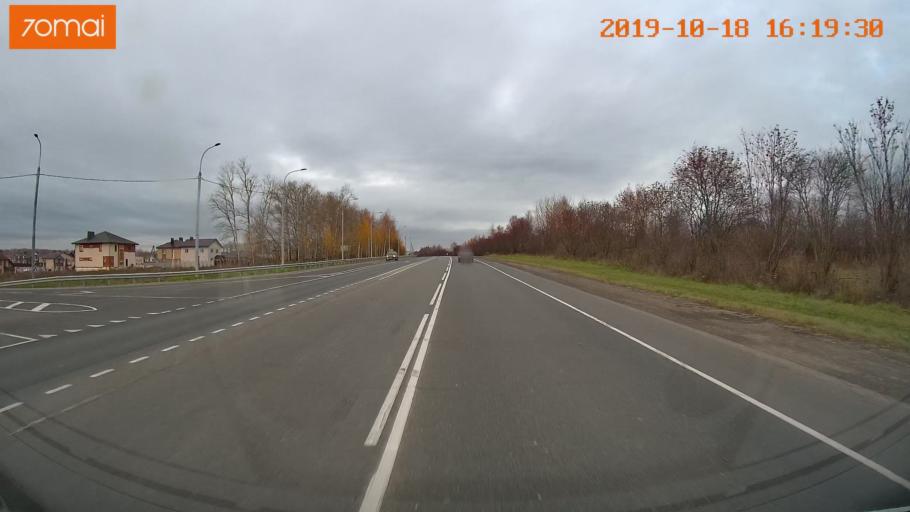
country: RU
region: Vladimir
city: Bogolyubovo
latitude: 56.1986
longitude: 40.4460
